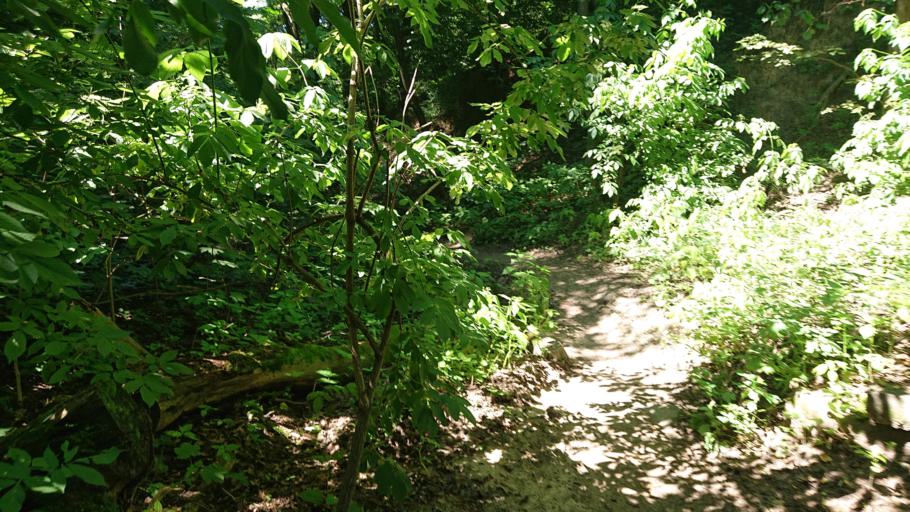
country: PL
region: Lublin Voivodeship
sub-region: Powiat pulawski
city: Kazimierz Dolny
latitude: 51.3263
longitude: 21.9678
